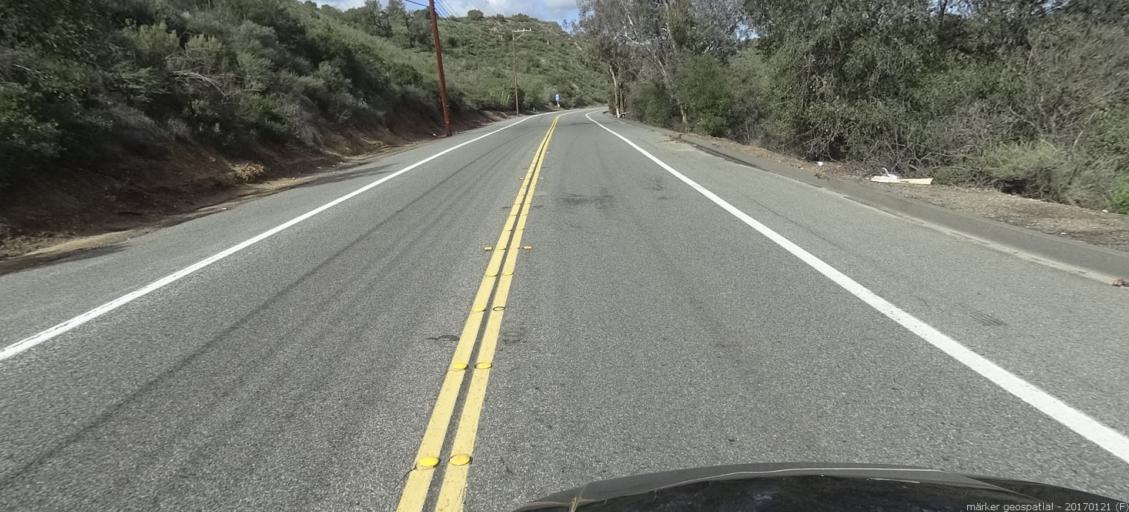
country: US
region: California
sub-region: Orange County
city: Foothill Ranch
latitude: 33.7484
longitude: -117.6786
